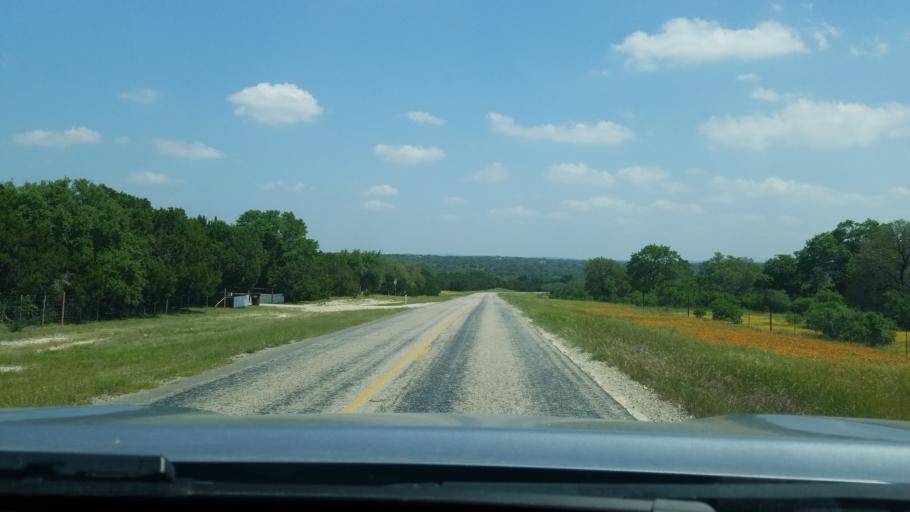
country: US
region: Texas
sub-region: Bexar County
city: Fair Oaks Ranch
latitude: 29.9022
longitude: -98.5656
